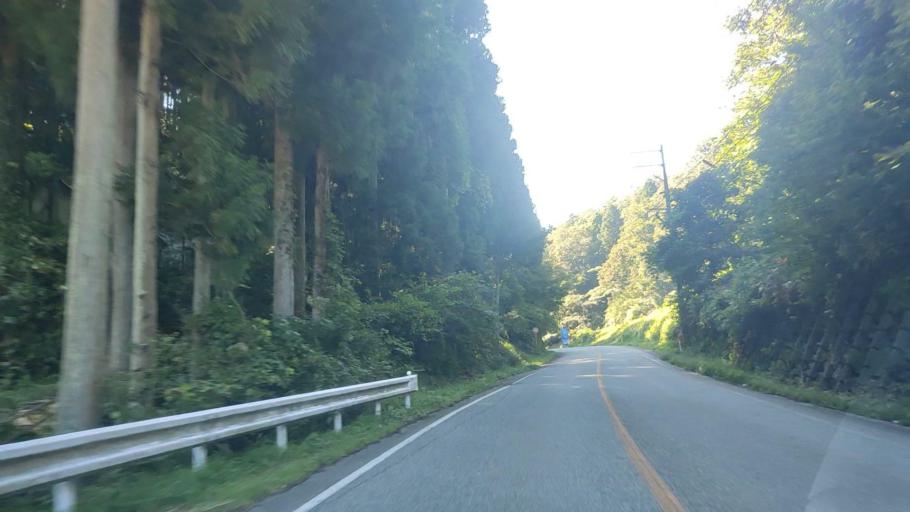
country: JP
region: Ishikawa
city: Nanao
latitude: 37.3211
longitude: 137.1756
